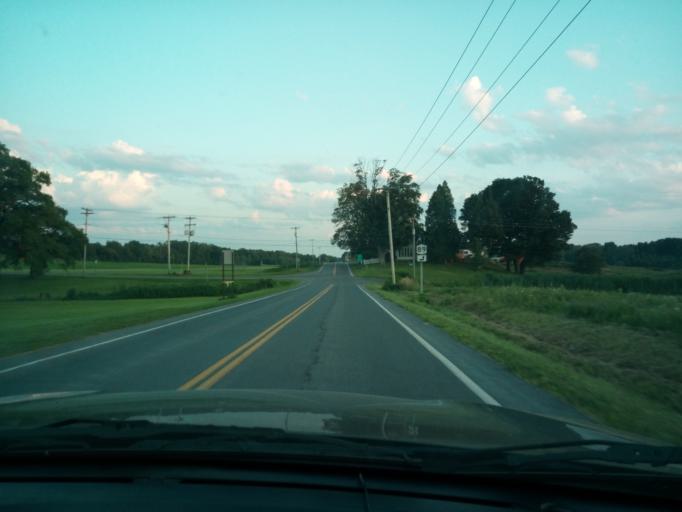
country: US
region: New York
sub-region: Seneca County
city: Bridgeport
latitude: 43.0228
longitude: -76.7701
